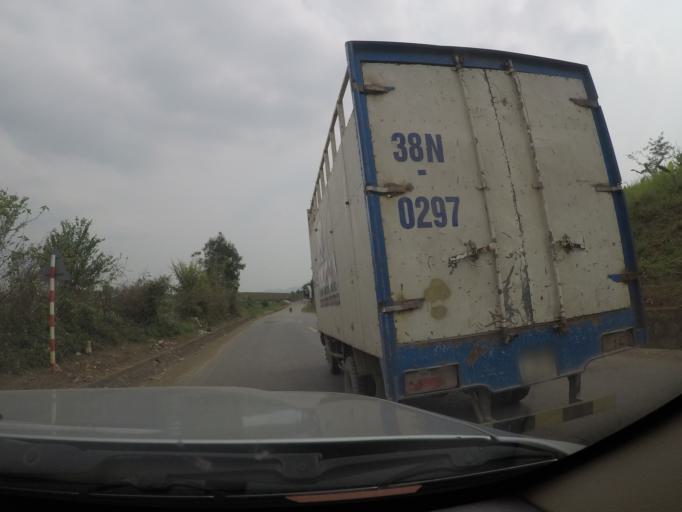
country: VN
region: Thanh Hoa
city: Thi Tran Ben Sung
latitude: 19.3844
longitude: 105.4601
